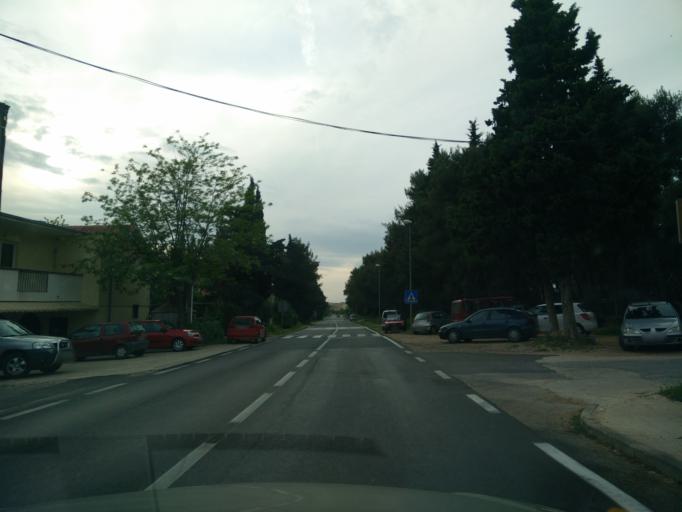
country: HR
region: Zadarska
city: Turanj
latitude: 43.9710
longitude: 15.4060
